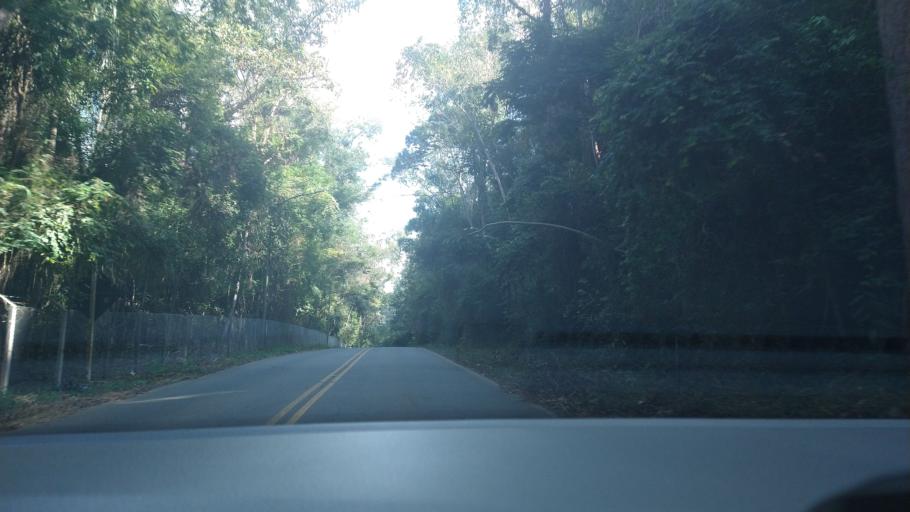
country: BR
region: Minas Gerais
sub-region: Vicosa
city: Vicosa
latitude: -20.7665
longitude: -42.8716
